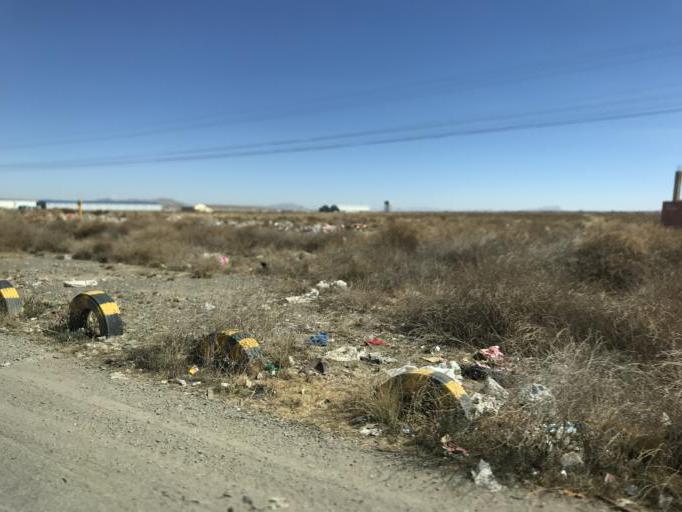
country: BO
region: La Paz
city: La Paz
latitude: -16.5193
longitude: -68.2913
